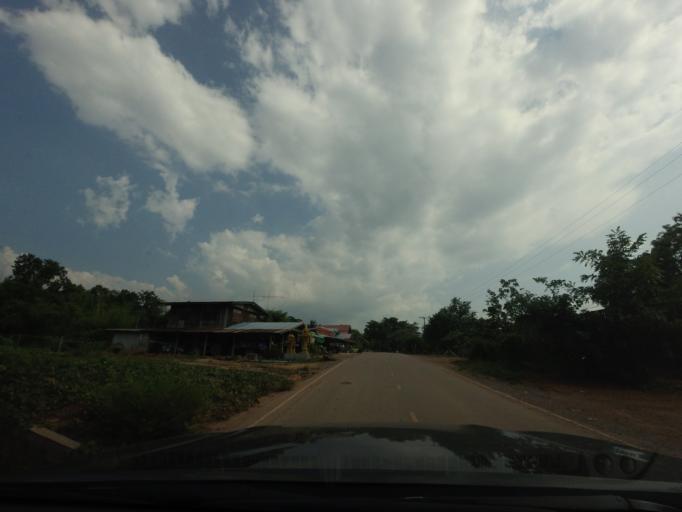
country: TH
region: Phitsanulok
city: Nakhon Thai
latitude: 17.0503
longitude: 100.9088
